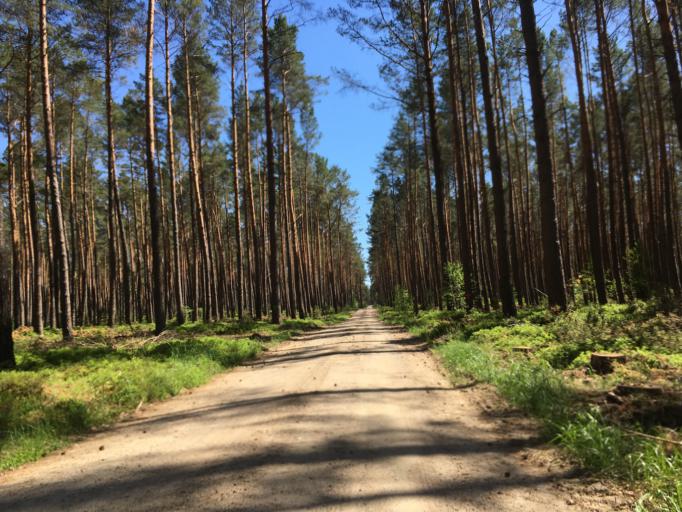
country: DE
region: Brandenburg
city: Friedrichswalde
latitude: 52.9776
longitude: 13.6302
